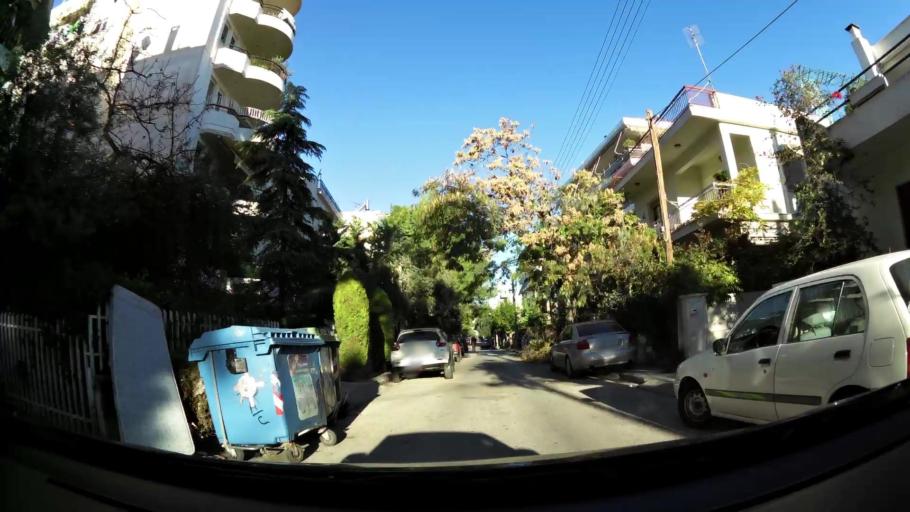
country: GR
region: Attica
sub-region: Nomarchia Athinas
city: Neo Psychiko
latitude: 38.0121
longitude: 23.7939
